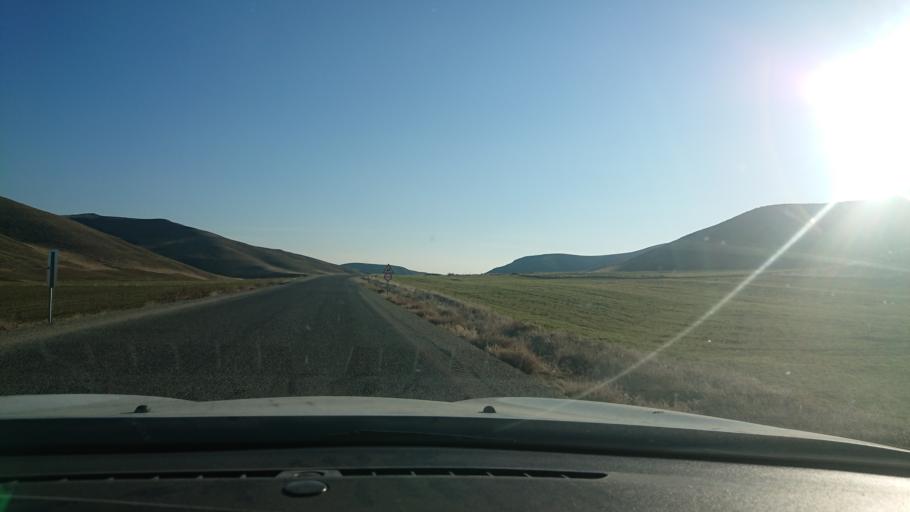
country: TR
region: Aksaray
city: Acipinar
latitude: 38.7041
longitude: 33.7552
